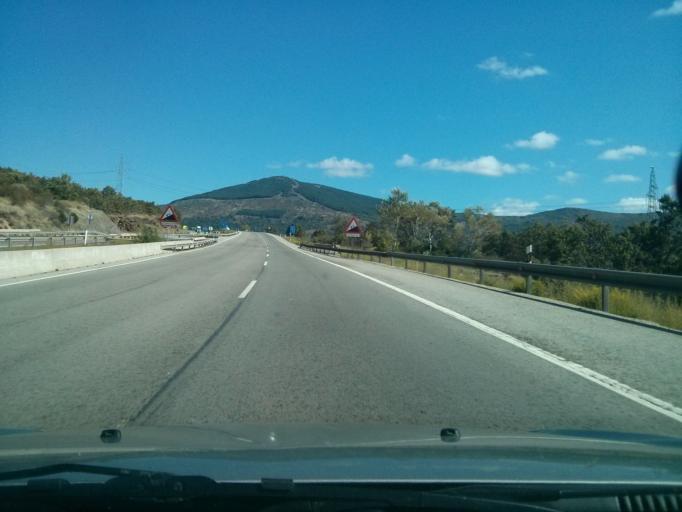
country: ES
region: Madrid
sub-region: Provincia de Madrid
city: Horcajo de la Sierra
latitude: 41.0794
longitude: -3.6003
